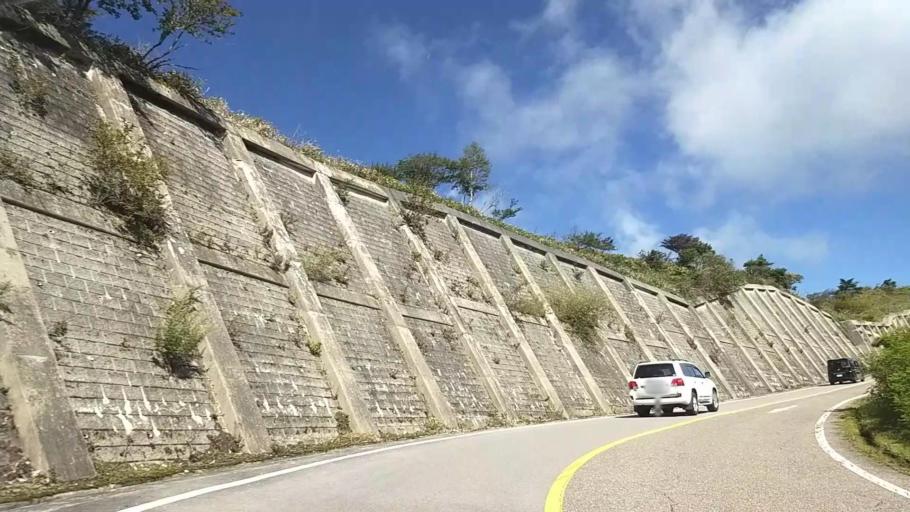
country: JP
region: Nagano
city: Suwa
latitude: 36.1529
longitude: 138.1353
